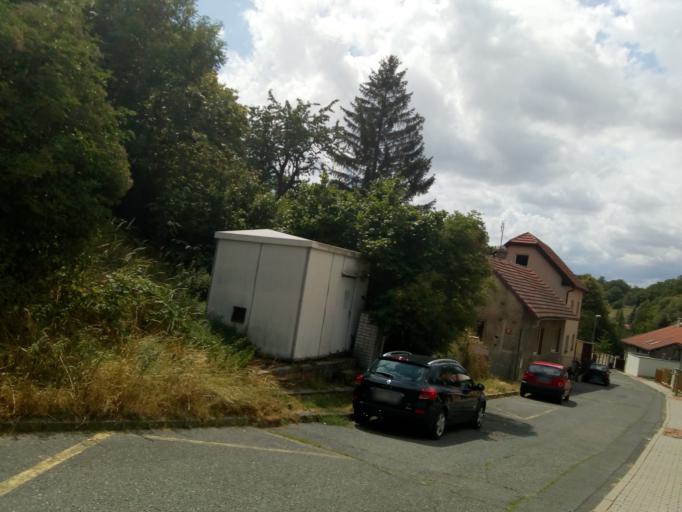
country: CZ
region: Central Bohemia
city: Tuchomerice
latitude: 50.1174
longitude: 14.2946
